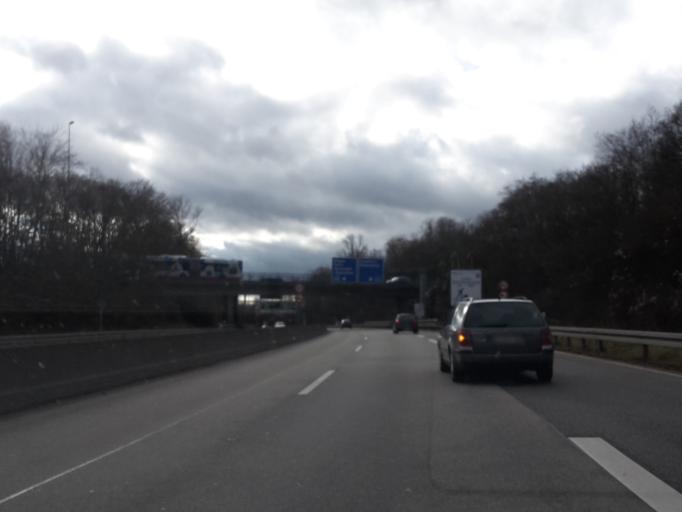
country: DE
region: Hesse
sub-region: Regierungsbezirk Darmstadt
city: Wiesbaden
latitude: 50.0603
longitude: 8.2141
